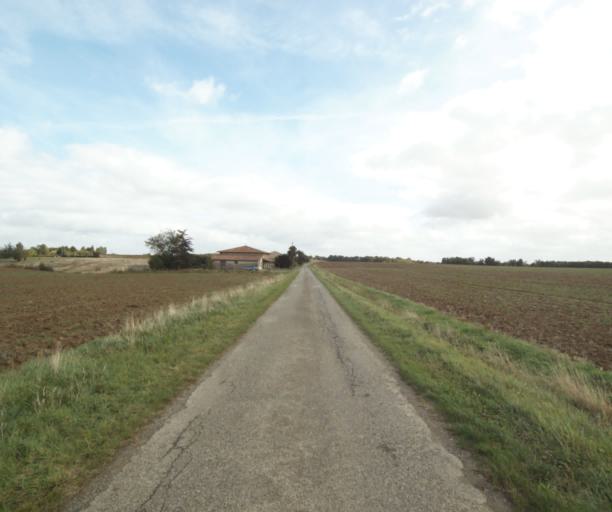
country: FR
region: Midi-Pyrenees
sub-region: Departement du Tarn-et-Garonne
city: Beaumont-de-Lomagne
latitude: 43.8730
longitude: 1.0893
